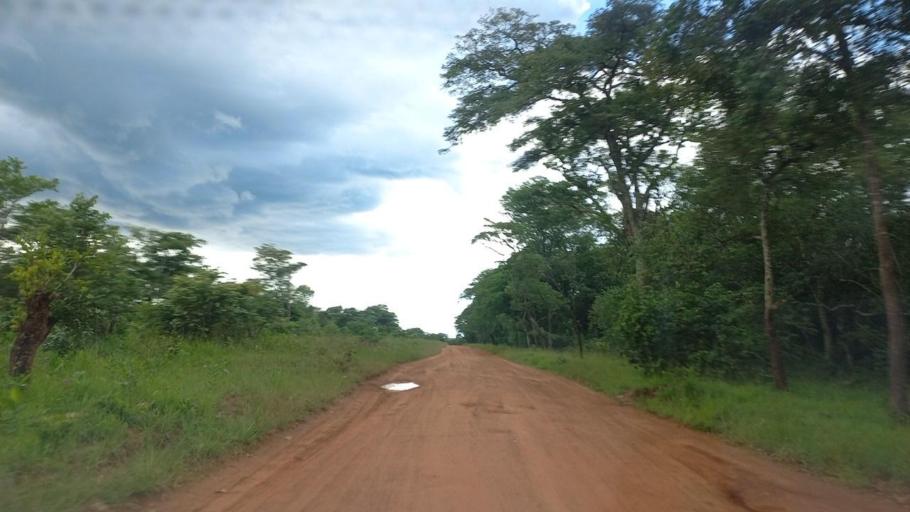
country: ZM
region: North-Western
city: Mwinilunga
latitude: -11.8247
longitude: 24.3685
